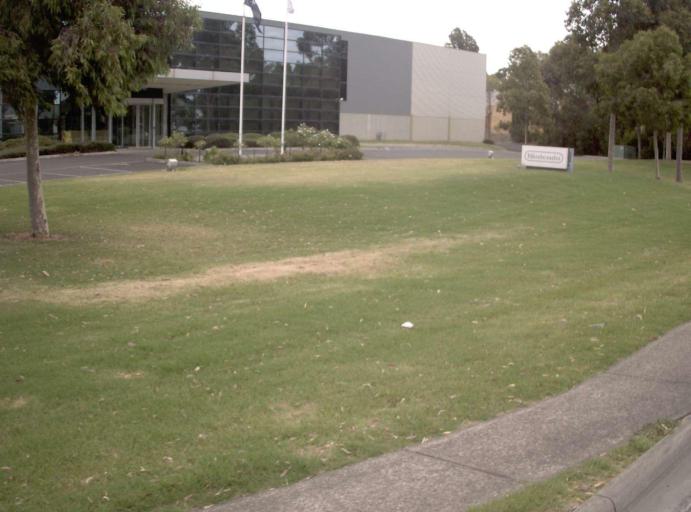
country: AU
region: Victoria
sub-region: Knox
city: Scoresby
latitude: -37.9019
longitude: 145.2348
